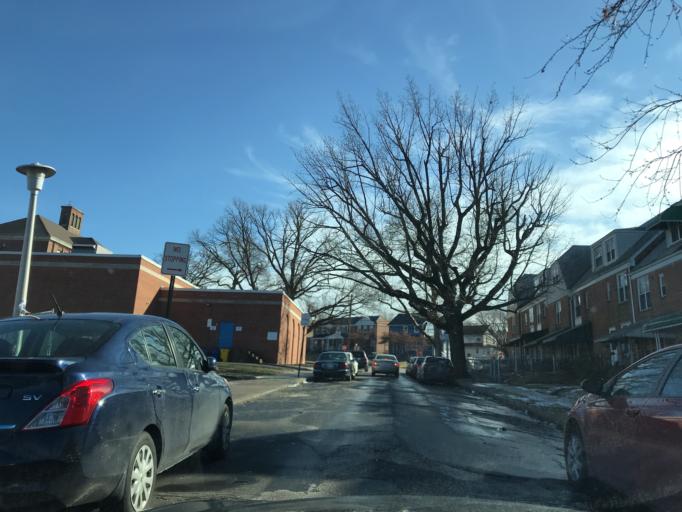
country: US
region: Maryland
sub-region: Baltimore County
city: Rosedale
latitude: 39.3215
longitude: -76.5676
